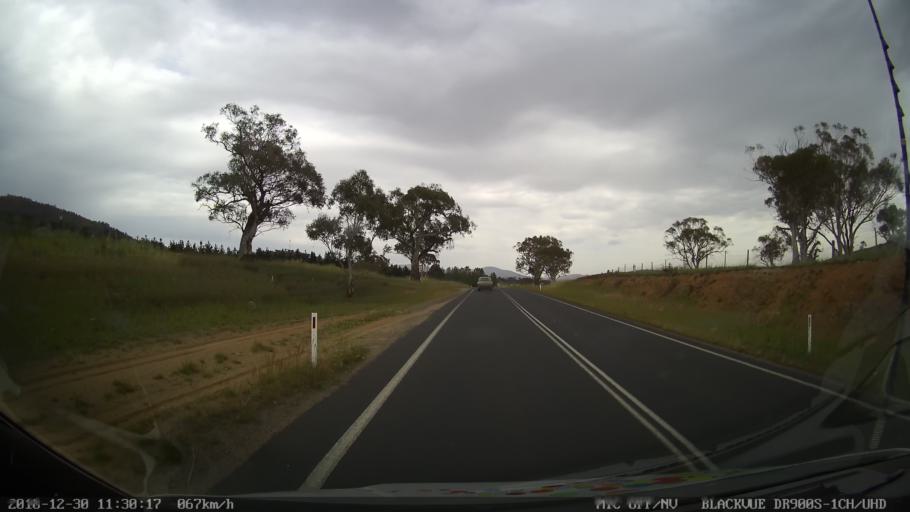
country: AU
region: New South Wales
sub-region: Snowy River
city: Jindabyne
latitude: -36.4439
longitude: 148.6059
